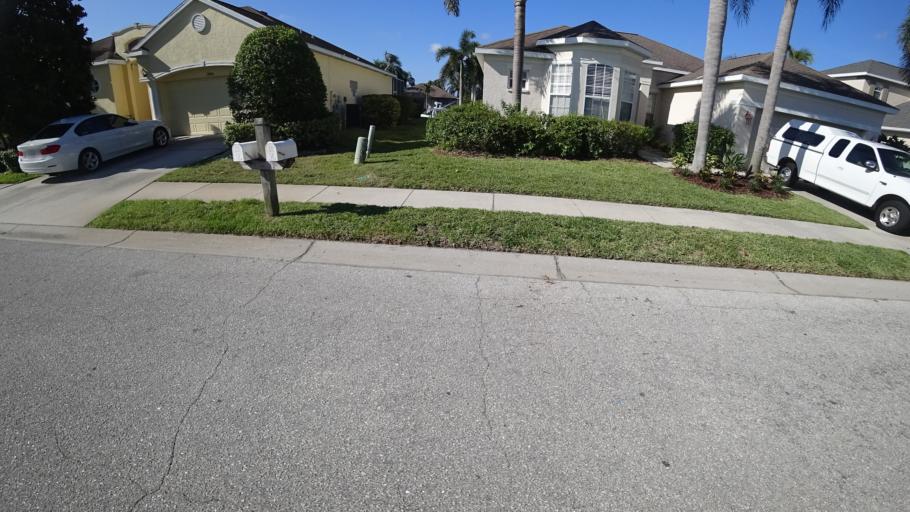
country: US
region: Florida
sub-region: Manatee County
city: Ellenton
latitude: 27.5056
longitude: -82.5150
